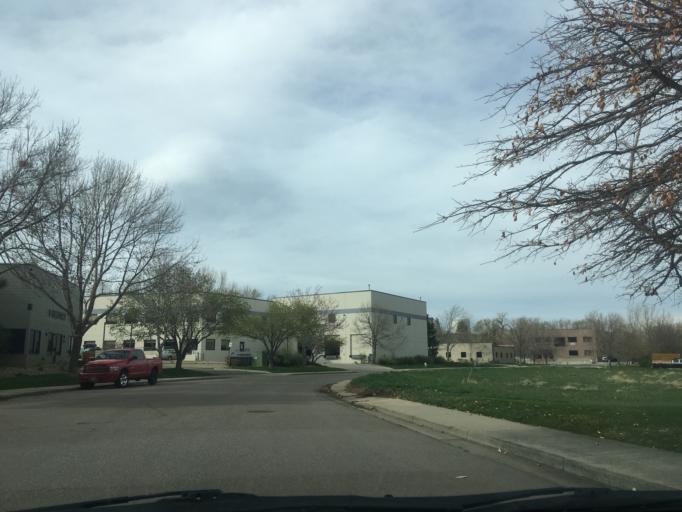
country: US
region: Colorado
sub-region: Boulder County
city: Boulder
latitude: 40.0311
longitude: -105.2282
